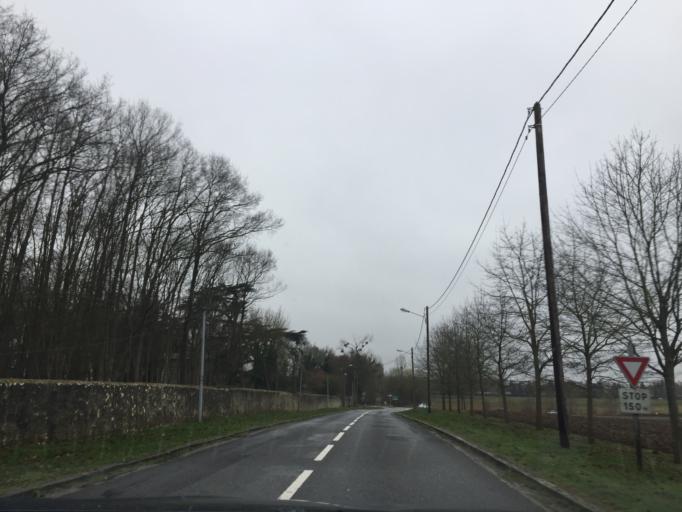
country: FR
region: Ile-de-France
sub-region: Departement de Seine-et-Marne
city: Coupvray
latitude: 48.8845
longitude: 2.7930
